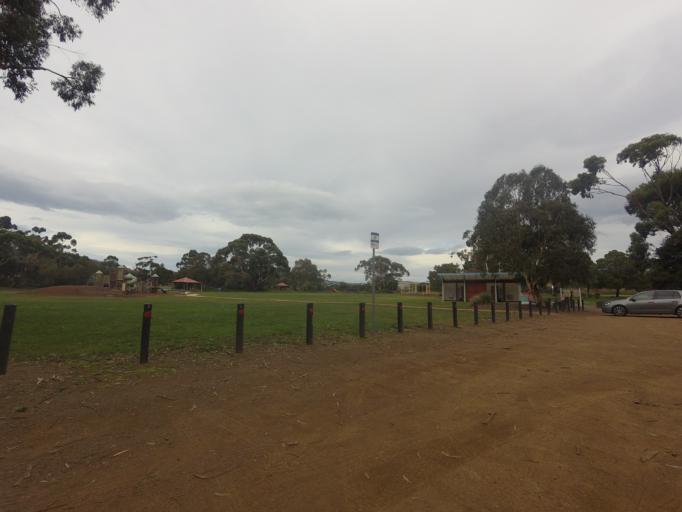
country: AU
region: Tasmania
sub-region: Clarence
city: Howrah
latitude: -42.8806
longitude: 147.3986
